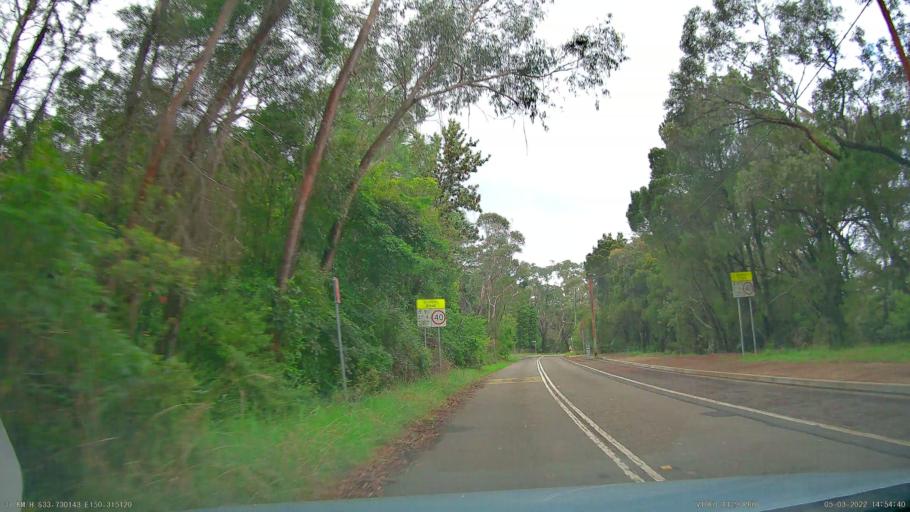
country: AU
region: New South Wales
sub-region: Blue Mountains Municipality
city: Katoomba
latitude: -33.7300
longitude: 150.3151
